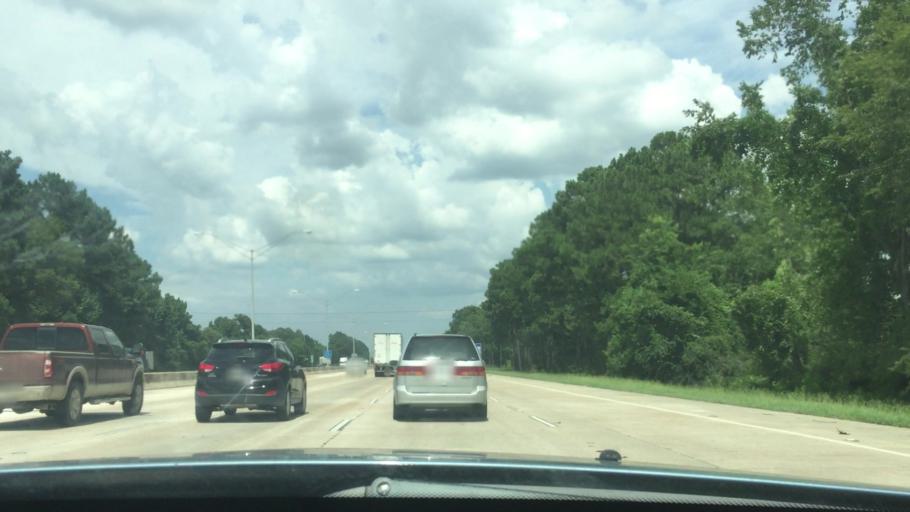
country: US
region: Louisiana
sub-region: East Baton Rouge Parish
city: Shenandoah
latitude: 30.4393
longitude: -91.0195
